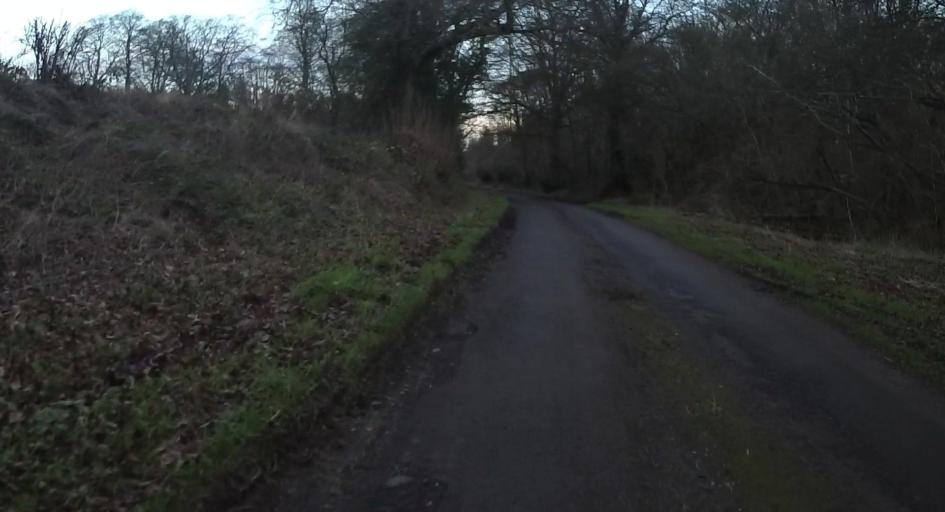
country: GB
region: England
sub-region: Hampshire
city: Four Marks
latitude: 51.0297
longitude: -1.1109
